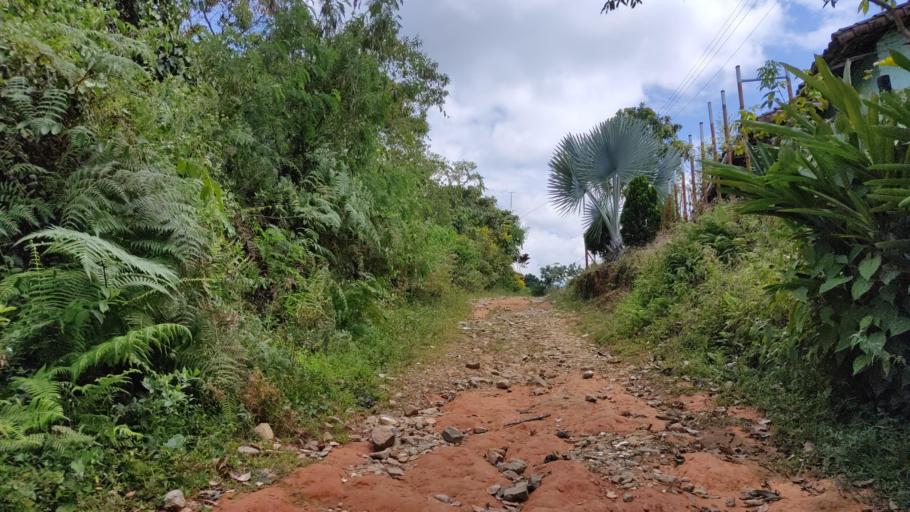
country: CO
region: Valle del Cauca
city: Jamundi
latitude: 3.2097
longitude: -76.6517
